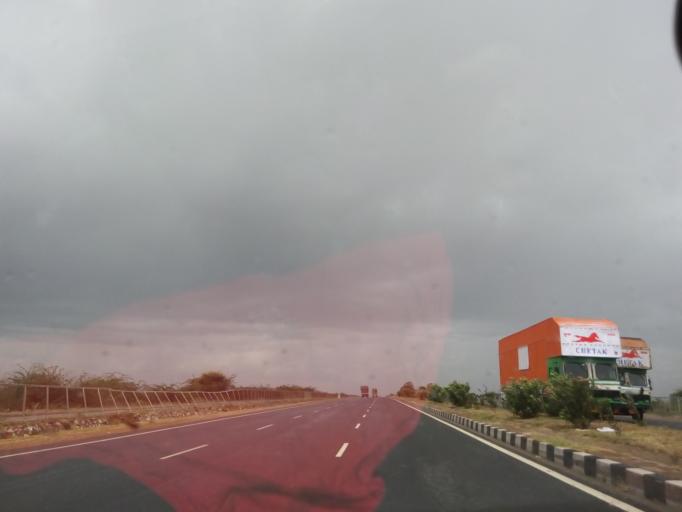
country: IN
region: Karnataka
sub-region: Chitradurga
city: Chitradurga
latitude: 14.1382
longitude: 76.4948
